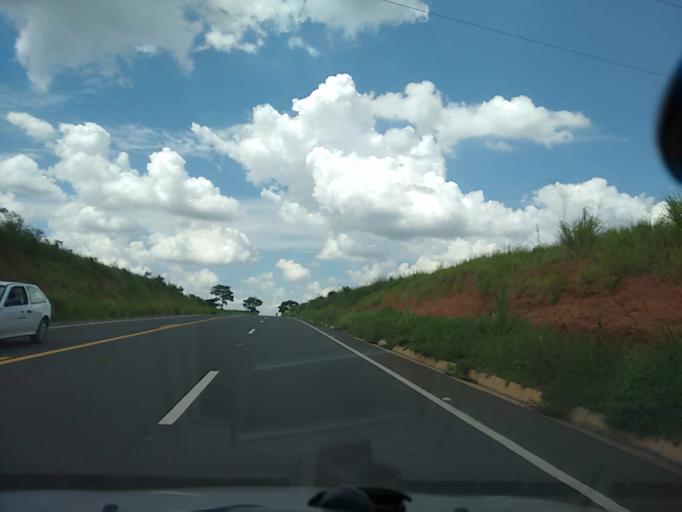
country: BR
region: Sao Paulo
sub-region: Osvaldo Cruz
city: Osvaldo Cruz
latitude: -21.8683
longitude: -50.8528
